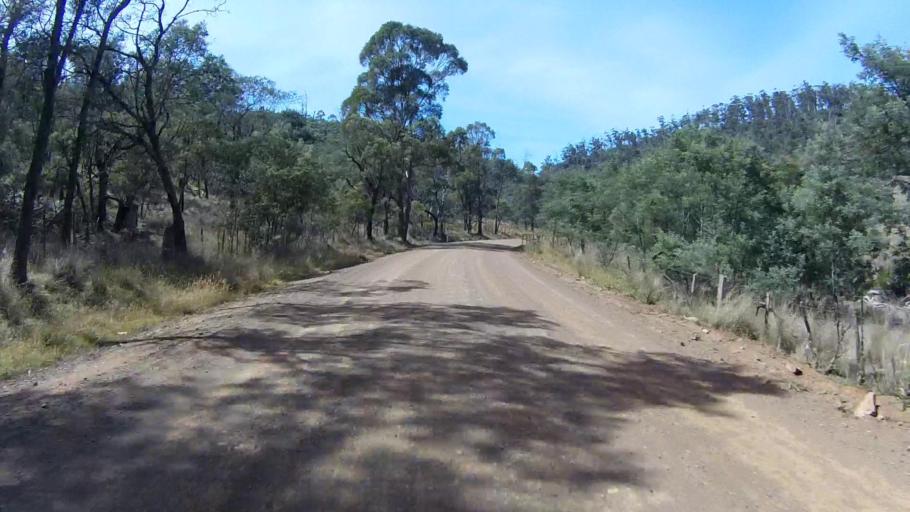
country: AU
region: Tasmania
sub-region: Sorell
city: Sorell
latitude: -42.6375
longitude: 147.7270
